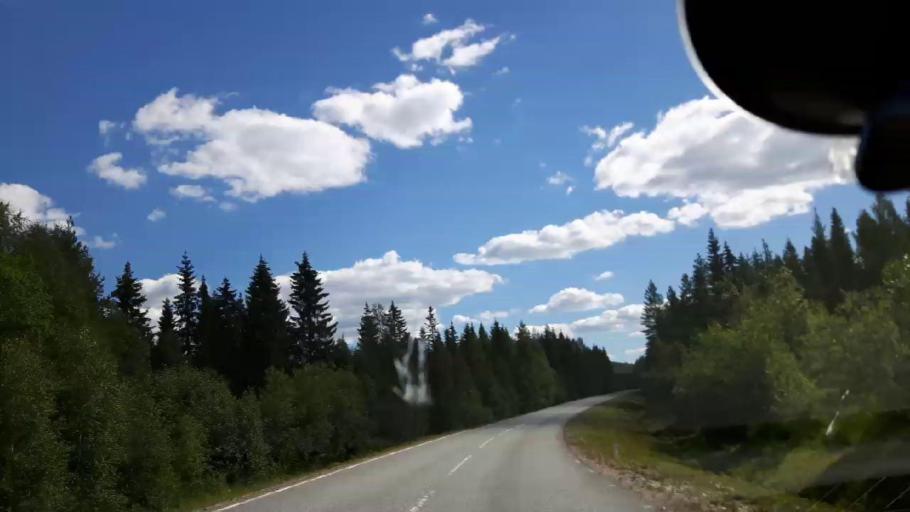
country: SE
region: Jaemtland
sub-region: Ragunda Kommun
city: Hammarstrand
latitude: 62.9554
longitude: 16.2078
